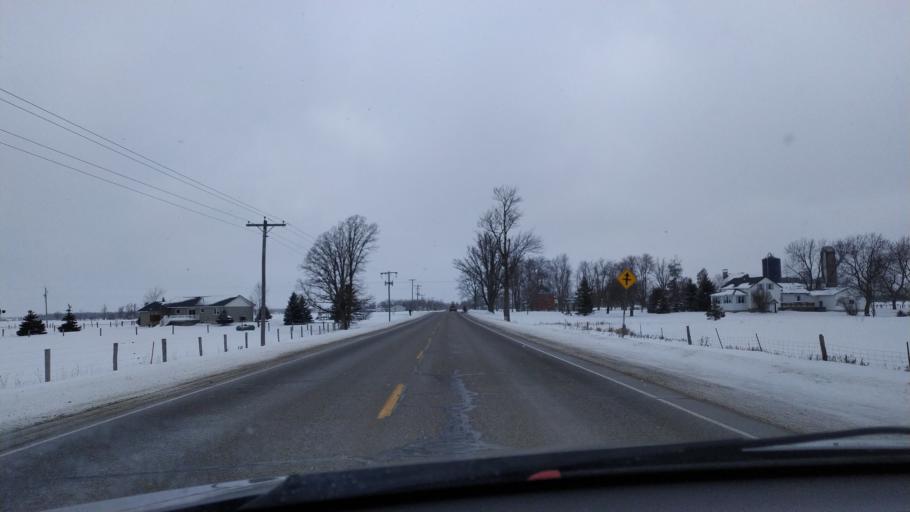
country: CA
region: Ontario
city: North Perth
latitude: 43.5806
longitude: -80.8562
